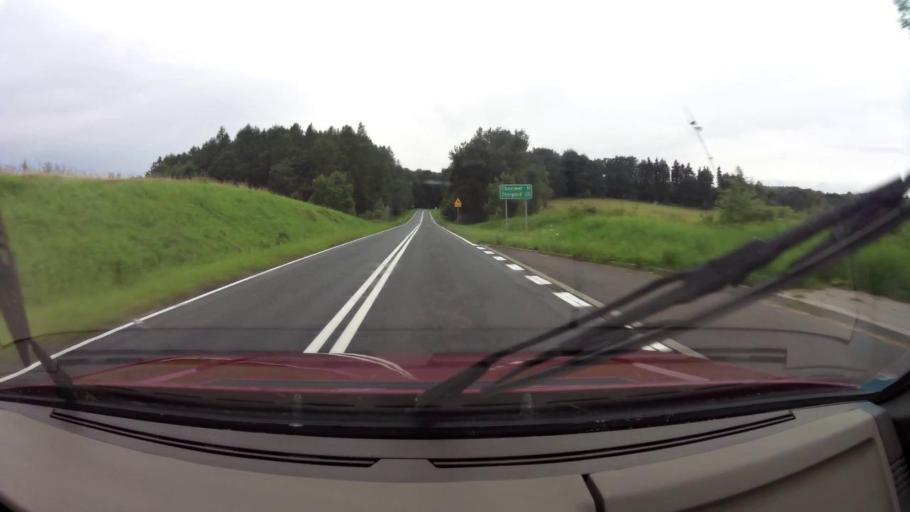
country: PL
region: West Pomeranian Voivodeship
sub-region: Powiat lobeski
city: Wegorzyno
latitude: 53.5076
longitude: 15.4496
